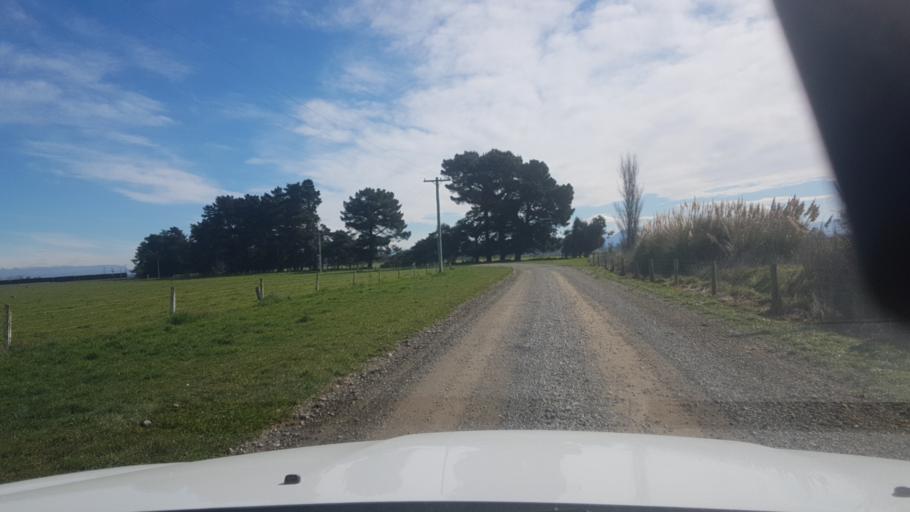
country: NZ
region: Canterbury
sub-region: Timaru District
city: Timaru
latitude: -44.2463
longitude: 171.3792
